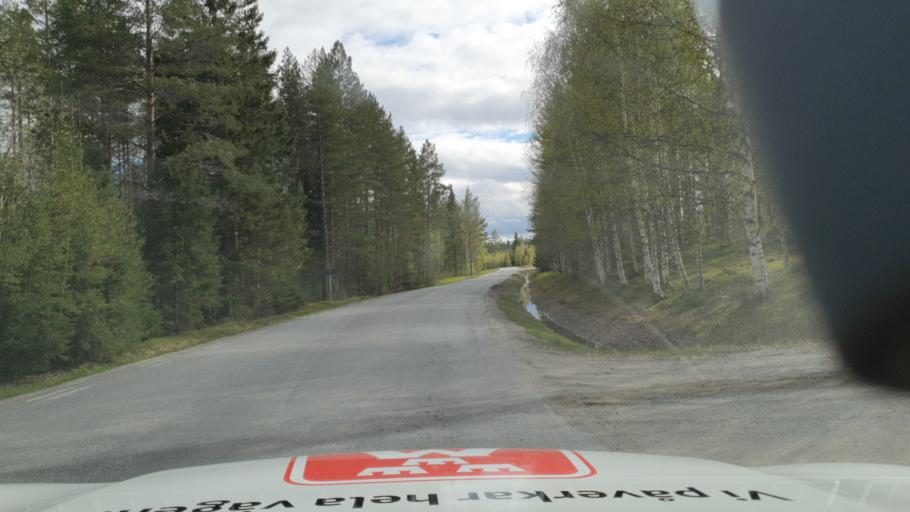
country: SE
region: Vaesterbotten
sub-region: Vannas Kommun
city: Vannasby
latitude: 64.0588
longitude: 20.0648
